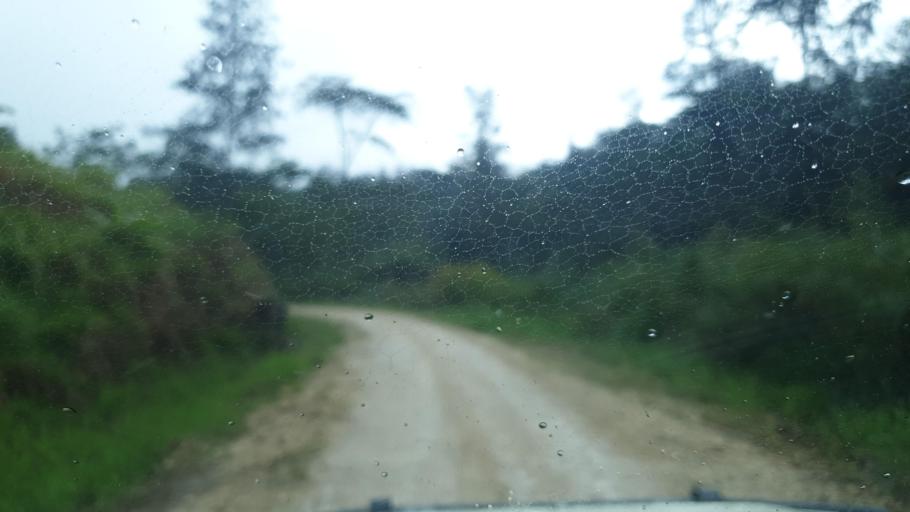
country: PG
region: Eastern Highlands
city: Goroka
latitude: -6.1959
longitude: 145.2115
